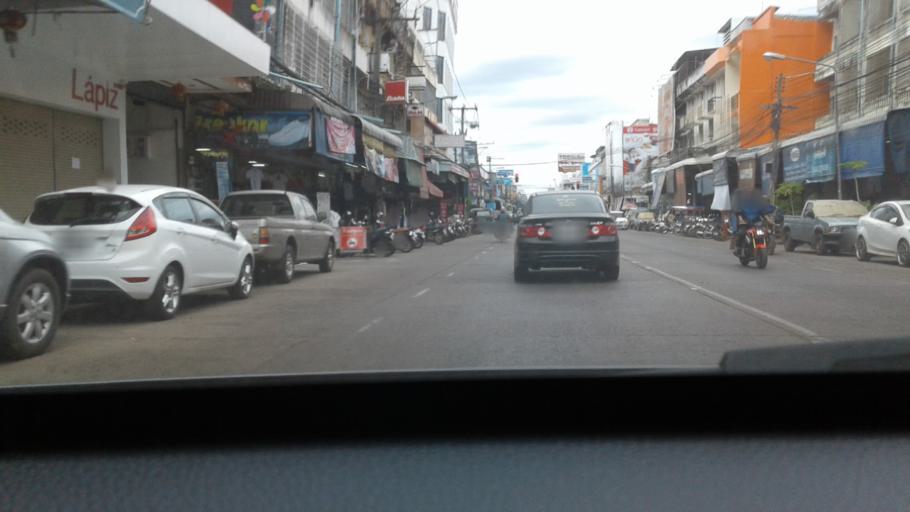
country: TH
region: Changwat Udon Thani
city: Udon Thani
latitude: 17.4049
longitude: 102.7928
